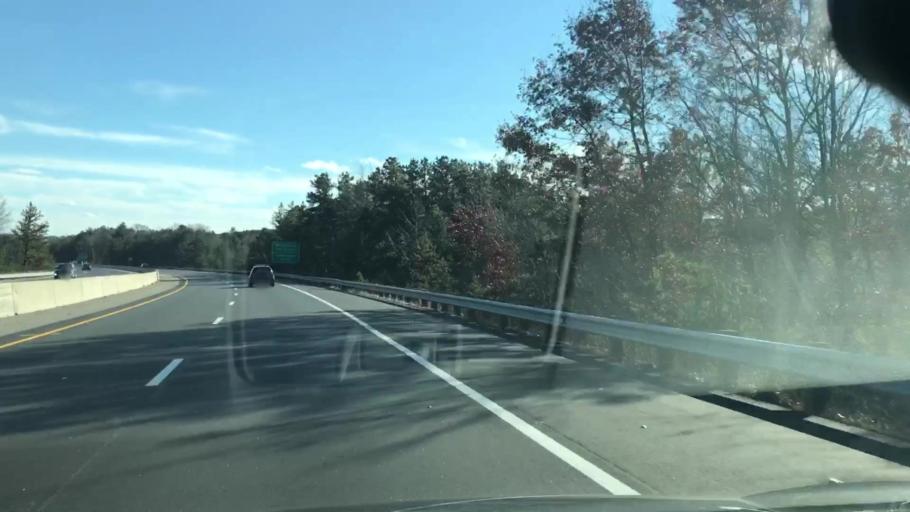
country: US
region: New Hampshire
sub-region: Hillsborough County
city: Pinardville
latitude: 43.0212
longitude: -71.4879
